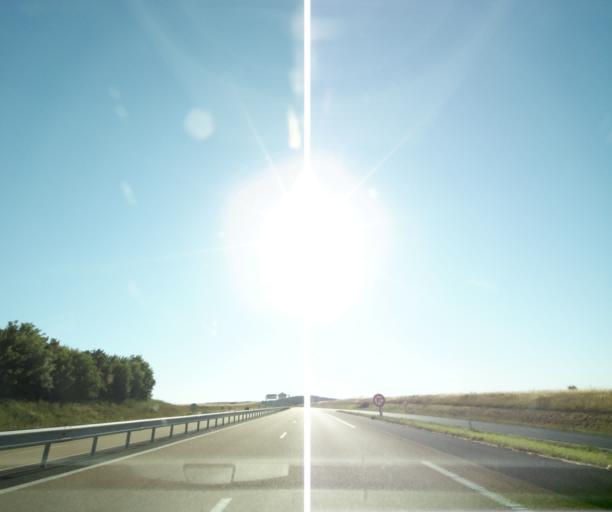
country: FR
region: Champagne-Ardenne
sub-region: Departement de l'Aube
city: Aix-en-Othe
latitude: 48.2412
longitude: 3.5998
